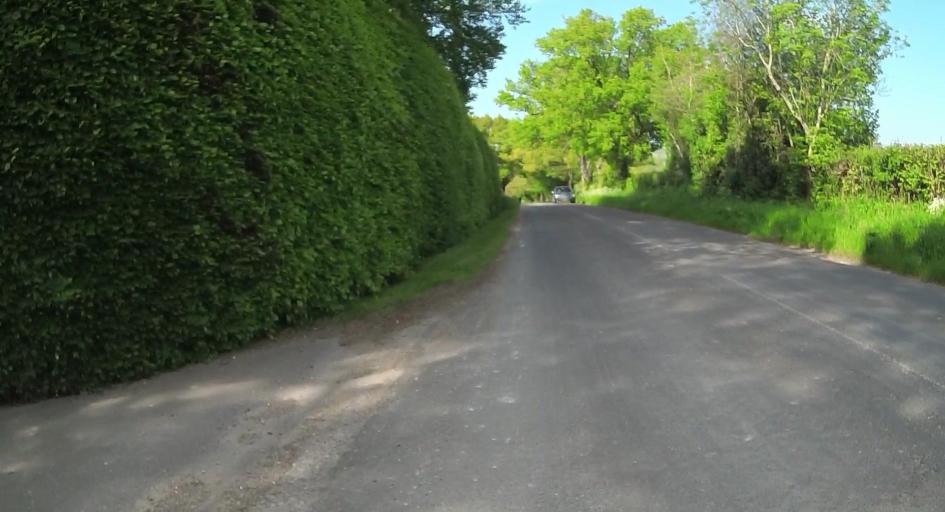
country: GB
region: England
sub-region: Hampshire
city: Four Marks
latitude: 51.1434
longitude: -1.0621
